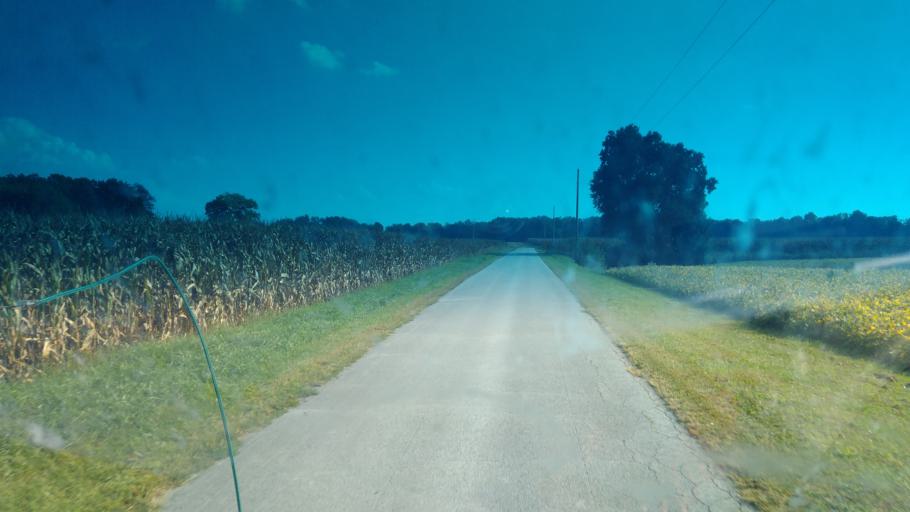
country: US
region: Ohio
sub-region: Wyandot County
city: Upper Sandusky
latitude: 40.9104
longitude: -83.2465
